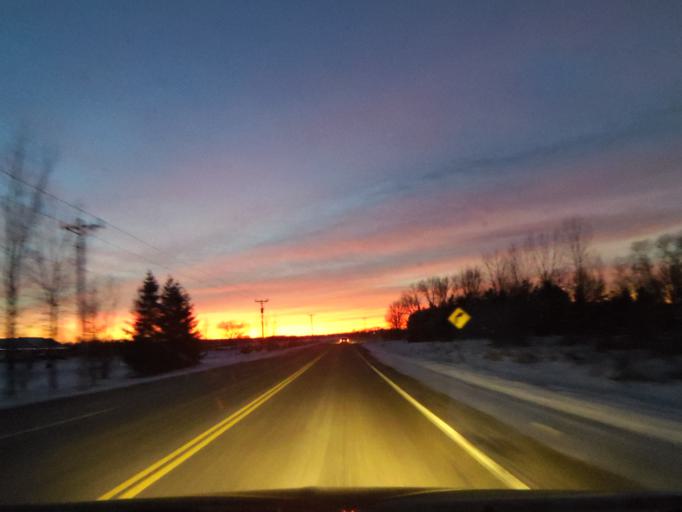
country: US
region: Minnesota
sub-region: Chisago County
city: Lindstrom
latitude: 45.3489
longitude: -92.8283
